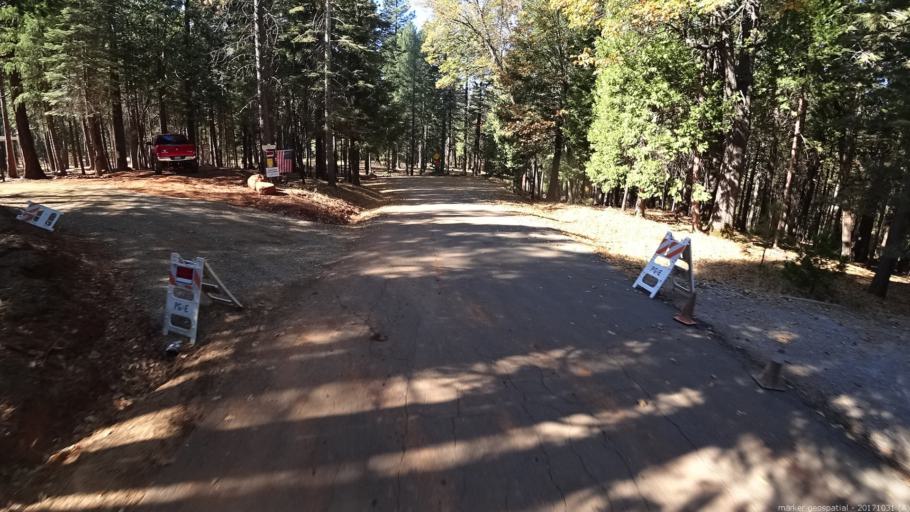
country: US
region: California
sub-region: Shasta County
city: Shingletown
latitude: 40.4855
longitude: -121.8980
